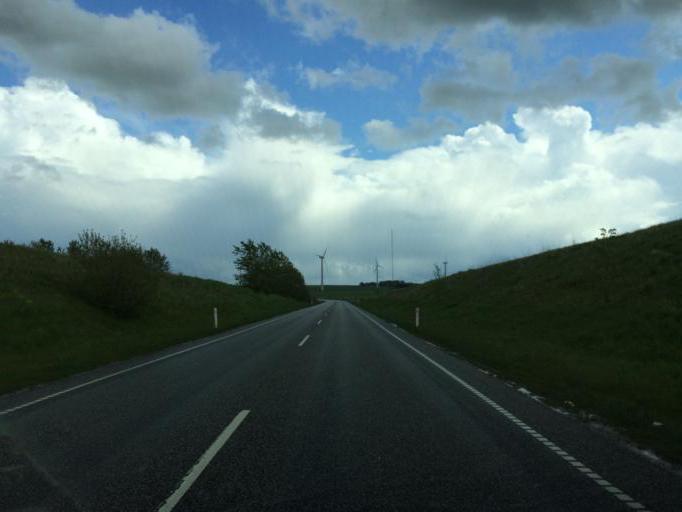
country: DK
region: Central Jutland
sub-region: Holstebro Kommune
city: Holstebro
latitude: 56.3789
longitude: 8.6390
